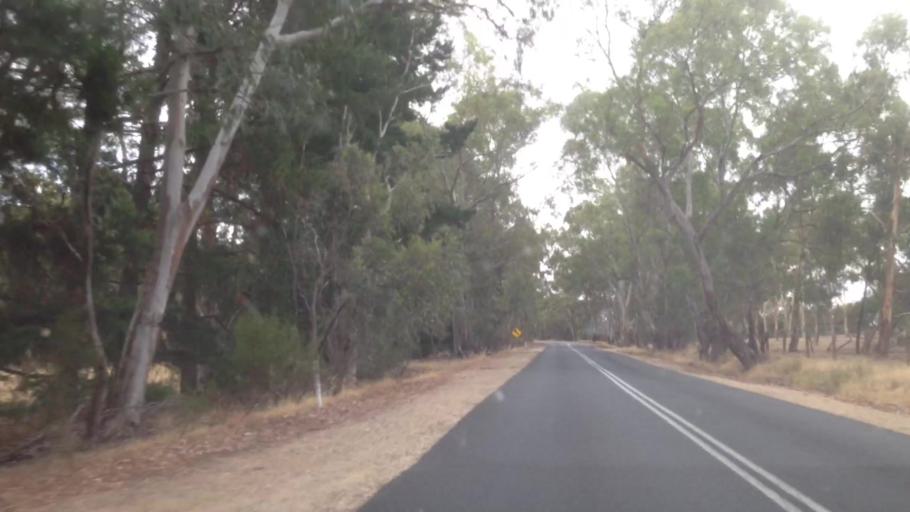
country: AU
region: South Australia
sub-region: Barossa
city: Williamstown
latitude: -34.6492
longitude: 138.8627
